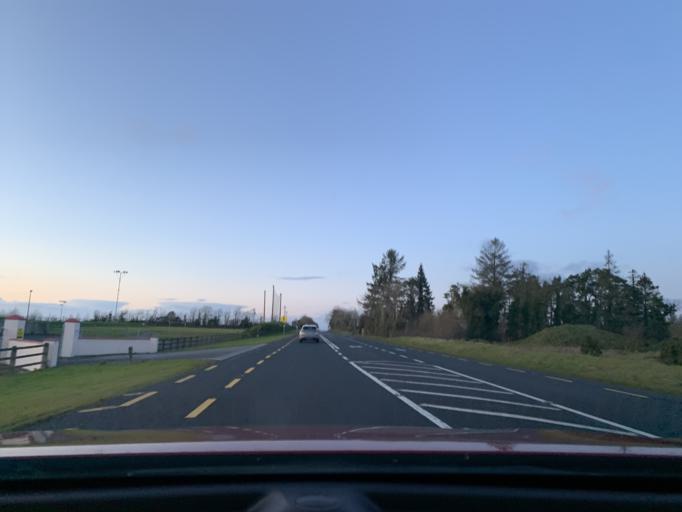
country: IE
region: Connaught
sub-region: County Leitrim
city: Carrick-on-Shannon
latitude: 53.8941
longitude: -7.9495
